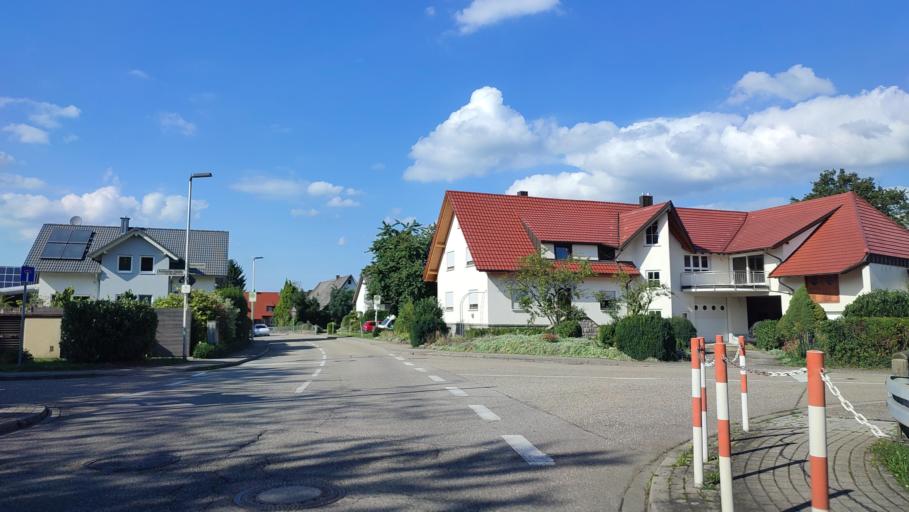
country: DE
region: Baden-Wuerttemberg
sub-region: Freiburg Region
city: Appenweier
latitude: 48.5450
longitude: 8.0176
